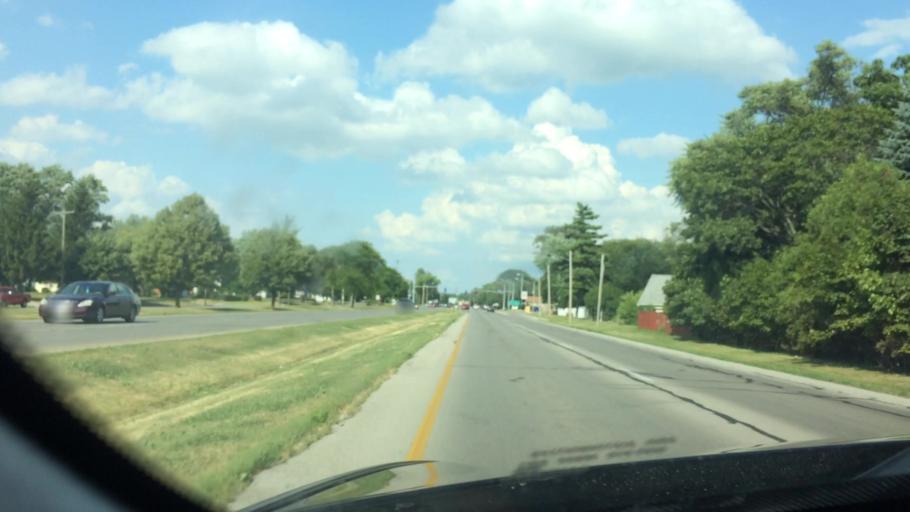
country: US
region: Ohio
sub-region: Wood County
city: Perrysburg
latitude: 41.5761
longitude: -83.6337
